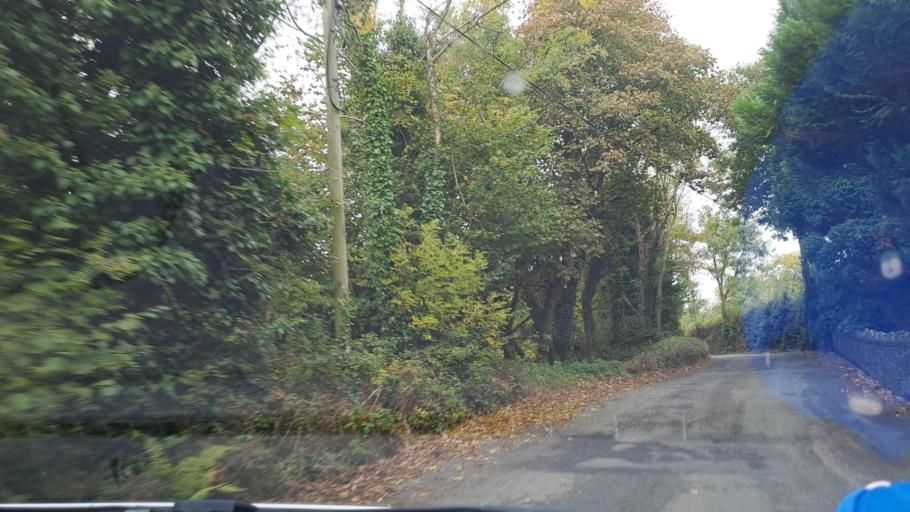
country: IE
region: Ulster
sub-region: An Cabhan
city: Kingscourt
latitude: 53.9415
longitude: -6.8033
